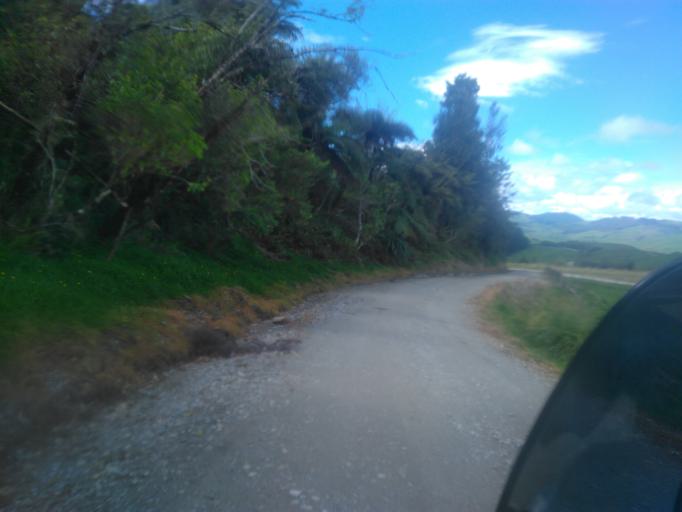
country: NZ
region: Hawke's Bay
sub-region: Wairoa District
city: Wairoa
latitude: -38.7765
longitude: 177.6271
